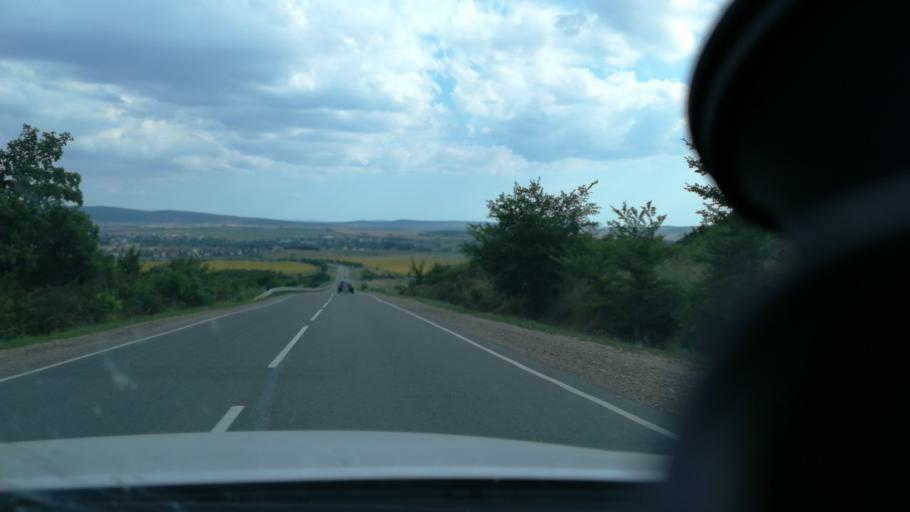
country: RU
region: Krasnodarskiy
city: Gostagayevskaya
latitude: 45.0512
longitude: 37.4710
